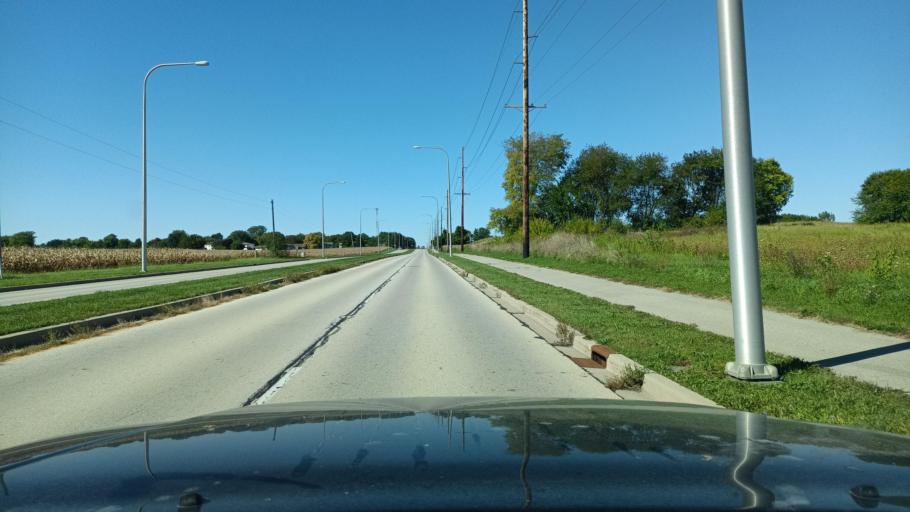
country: US
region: Illinois
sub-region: Champaign County
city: Urbana
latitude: 40.0840
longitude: -88.1750
